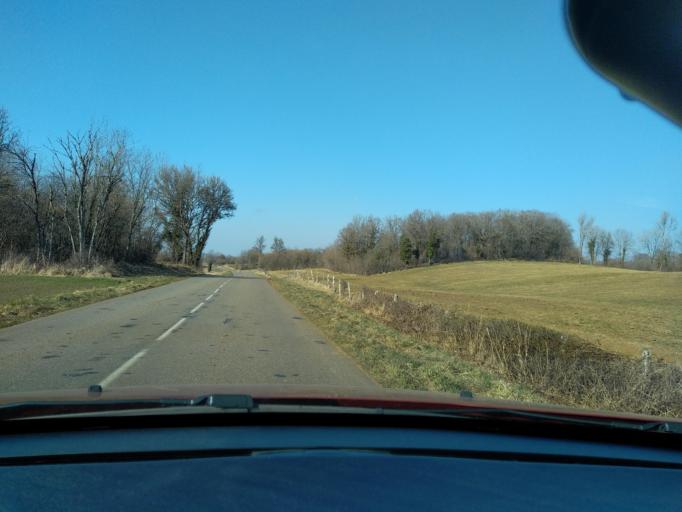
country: FR
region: Franche-Comte
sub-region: Departement du Jura
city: Perrigny
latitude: 46.6178
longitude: 5.6415
